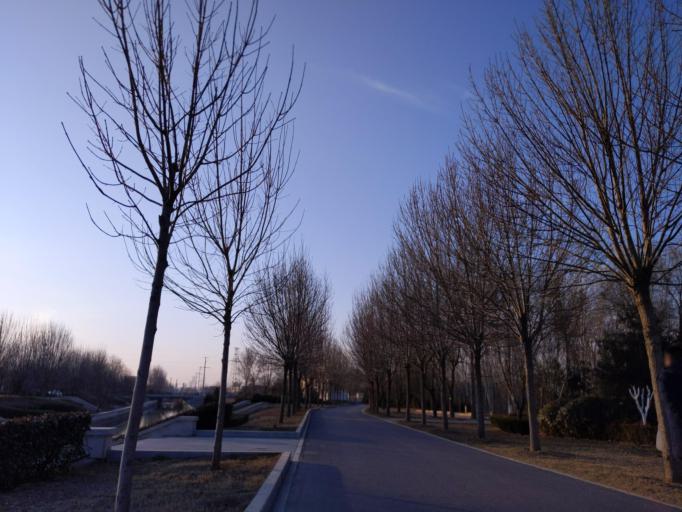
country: CN
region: Henan Sheng
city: Puyang
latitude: 35.7702
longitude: 114.9973
